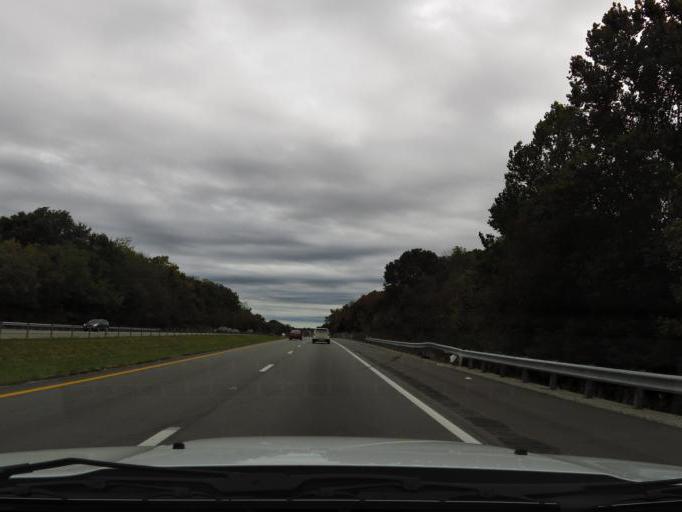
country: US
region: Kentucky
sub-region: Rockcastle County
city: Mount Vernon
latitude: 37.4022
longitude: -84.3385
